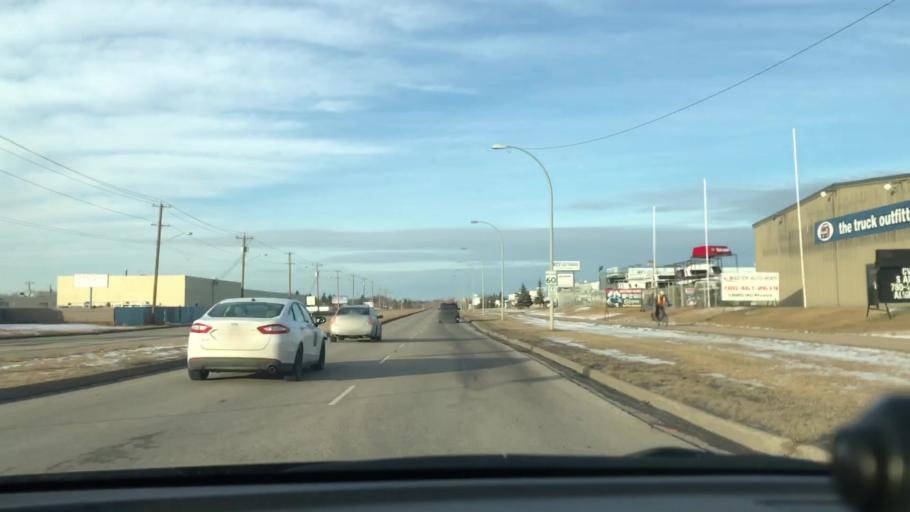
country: CA
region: Alberta
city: Edmonton
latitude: 53.4941
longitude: -113.4670
